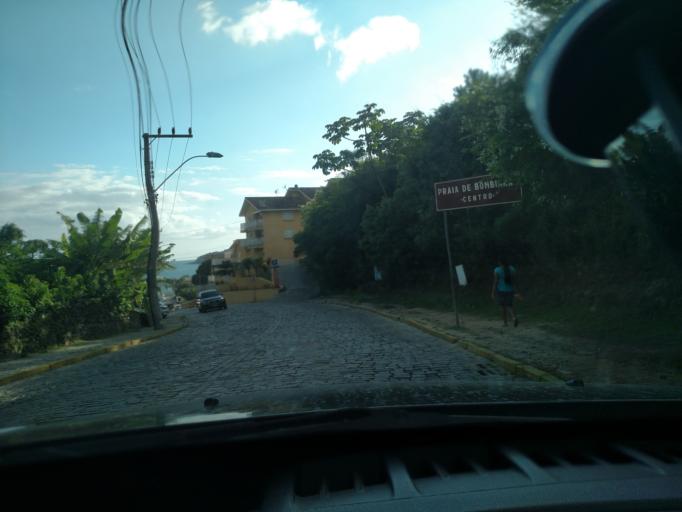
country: BR
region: Santa Catarina
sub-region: Porto Belo
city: Porto Belo
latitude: -27.1491
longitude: -48.4973
